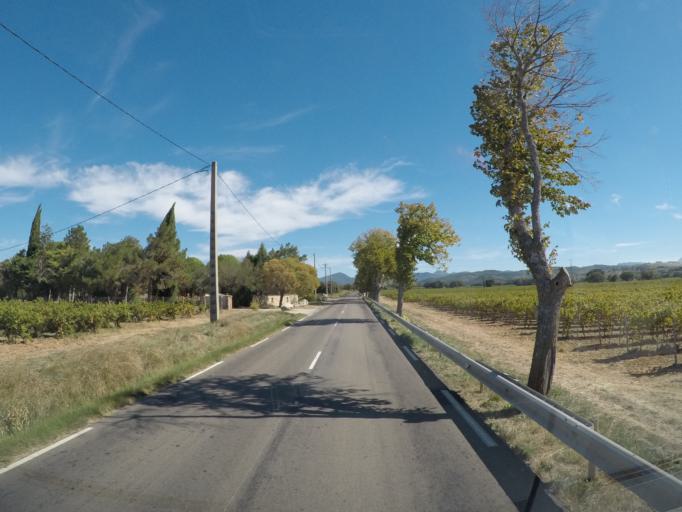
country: FR
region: Provence-Alpes-Cote d'Azur
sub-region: Departement du Vaucluse
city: Visan
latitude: 44.2927
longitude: 4.9925
